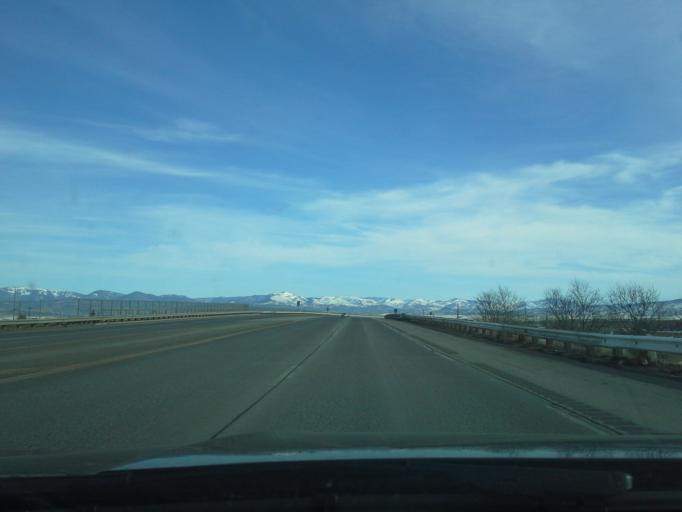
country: US
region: Montana
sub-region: Lewis and Clark County
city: East Helena
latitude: 46.5907
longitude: -111.9483
